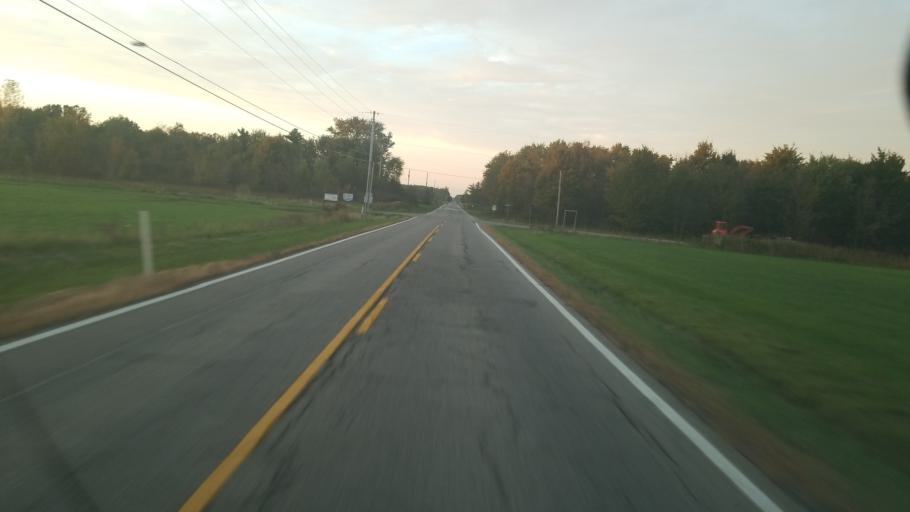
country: US
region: Ohio
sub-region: Ashtabula County
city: Andover
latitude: 41.6347
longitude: -80.6668
